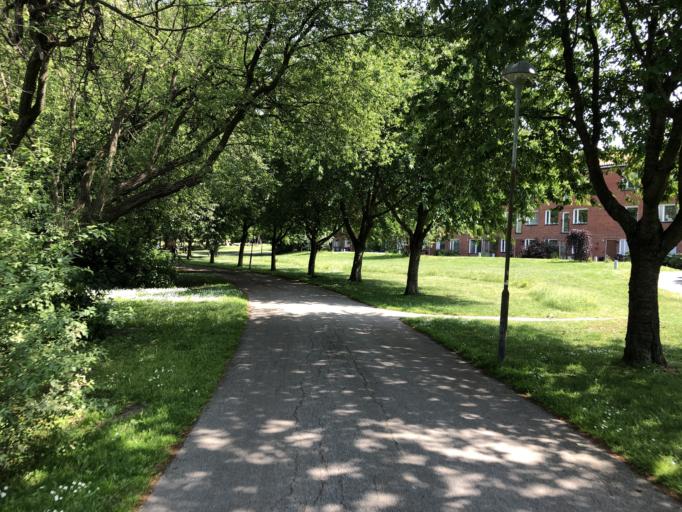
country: SE
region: Skane
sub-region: Lunds Kommun
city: Lund
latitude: 55.7191
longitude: 13.1873
